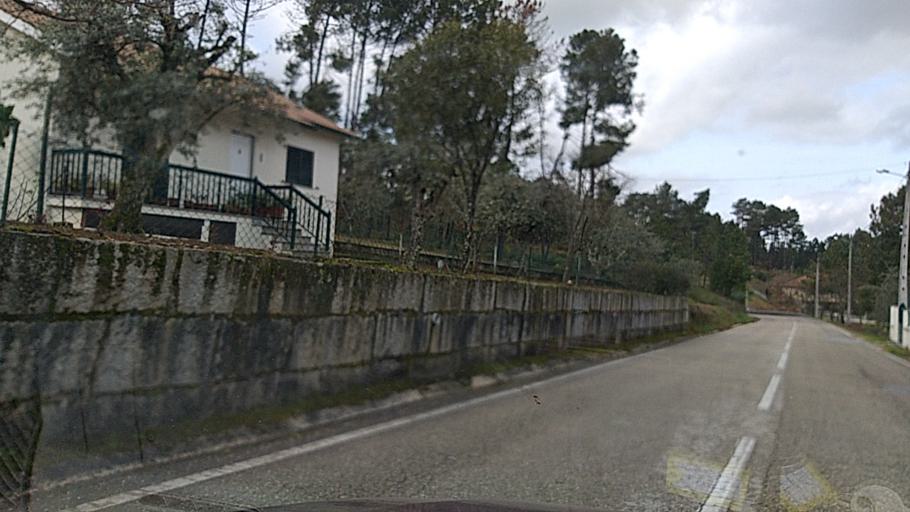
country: PT
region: Viseu
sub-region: Satao
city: Satao
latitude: 40.6575
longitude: -7.6613
